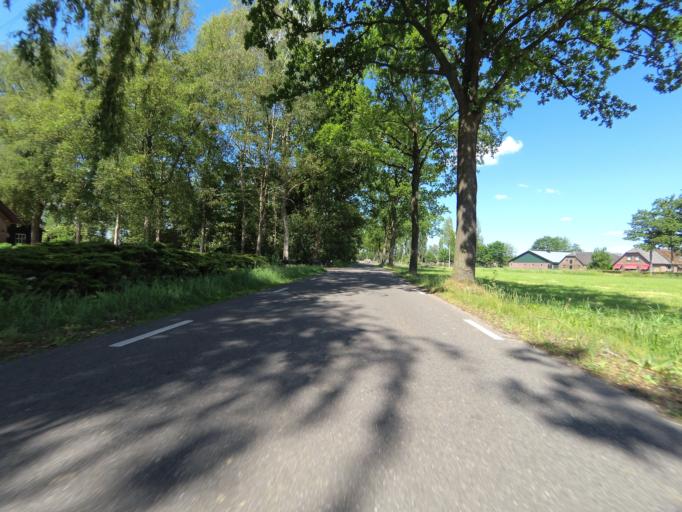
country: NL
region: Gelderland
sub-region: Gemeente Ede
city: Harskamp
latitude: 52.1414
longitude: 5.7371
